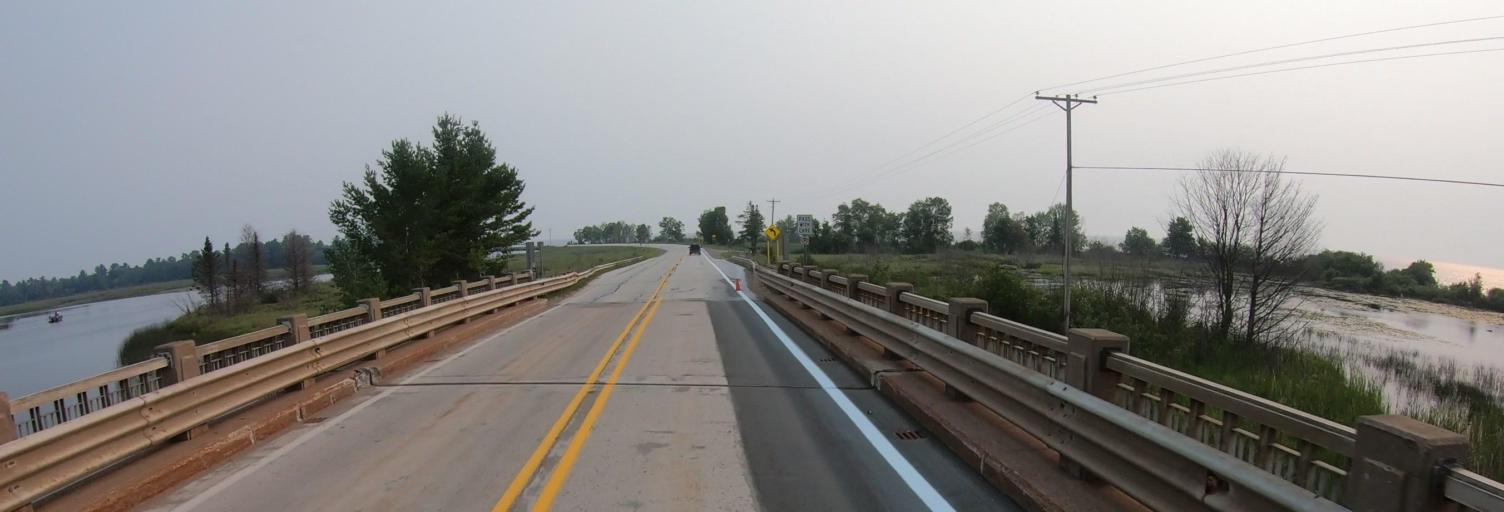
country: US
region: Michigan
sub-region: Luce County
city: Newberry
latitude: 46.5563
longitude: -85.0316
